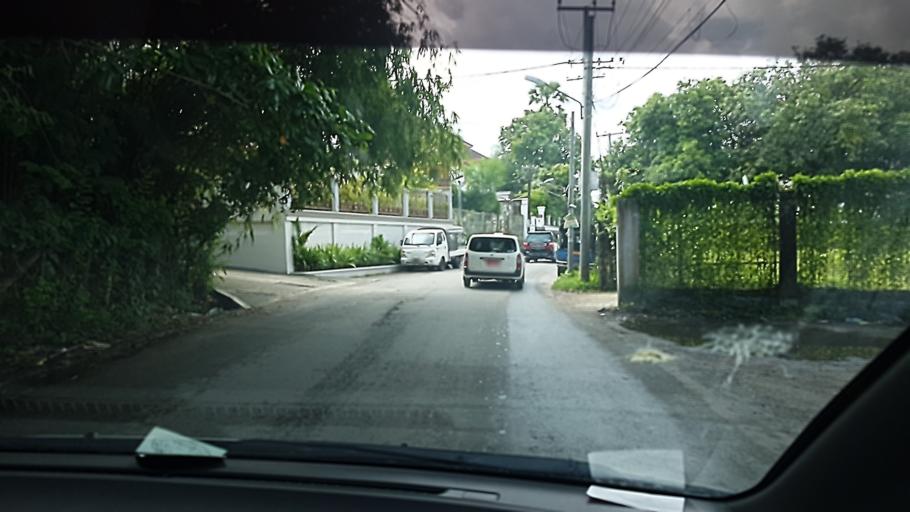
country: MM
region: Yangon
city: Yangon
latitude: 16.8165
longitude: 96.1479
